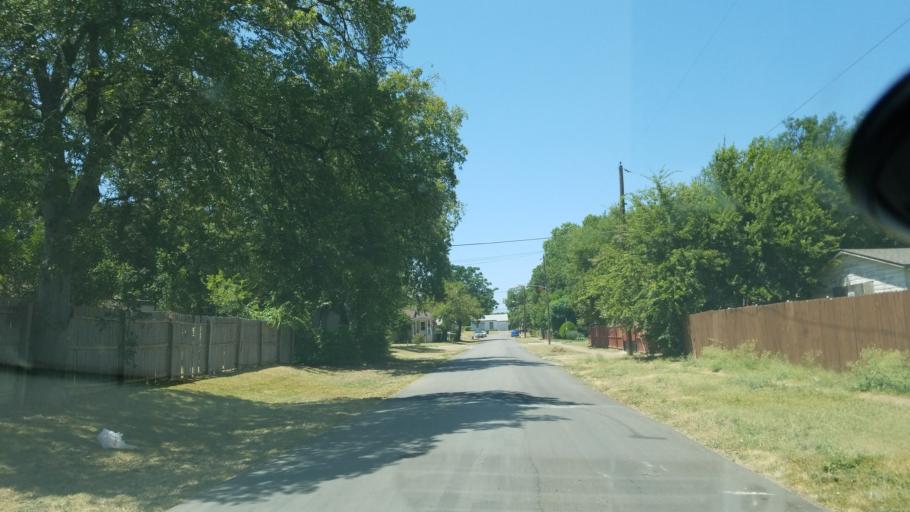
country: US
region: Texas
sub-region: Dallas County
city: Cockrell Hill
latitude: 32.7319
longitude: -96.8827
